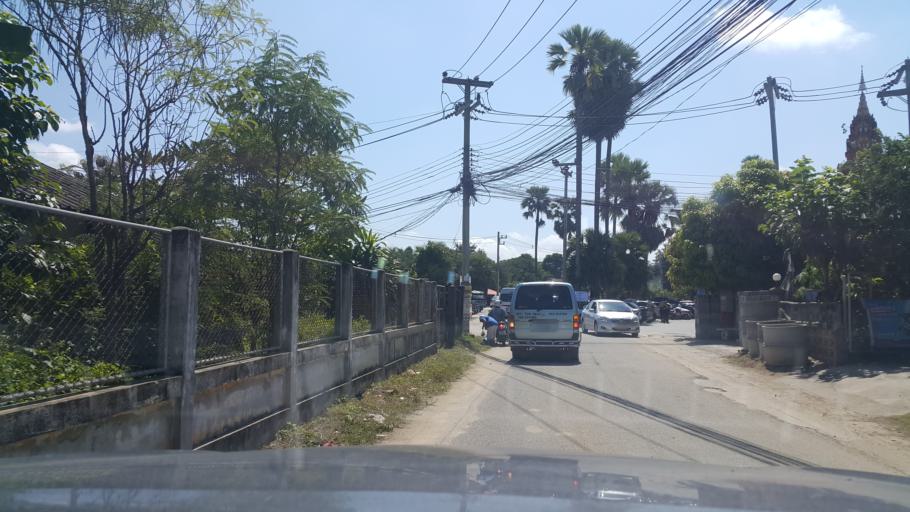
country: TH
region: Chiang Mai
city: San Sai
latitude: 18.9141
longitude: 98.9681
